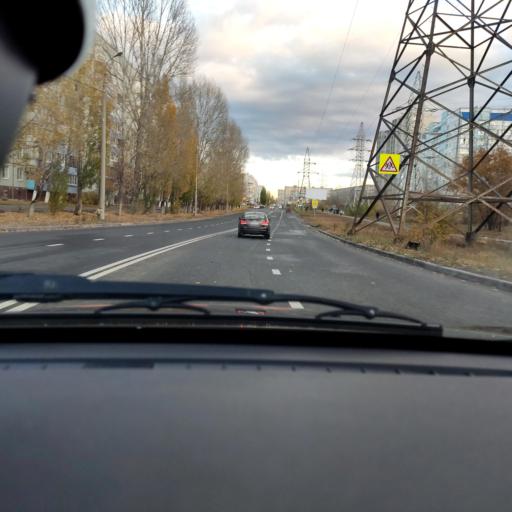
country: RU
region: Samara
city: Zhigulevsk
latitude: 53.4751
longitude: 49.5183
